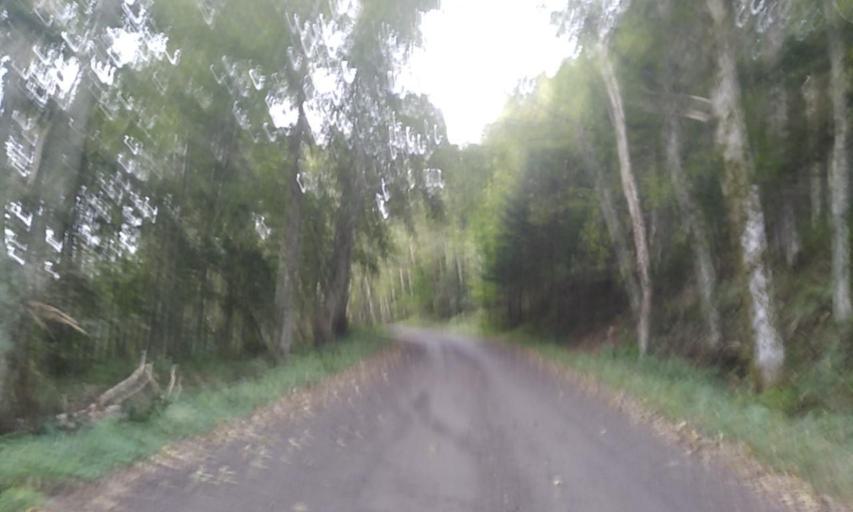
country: JP
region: Hokkaido
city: Abashiri
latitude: 43.6571
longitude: 144.5493
